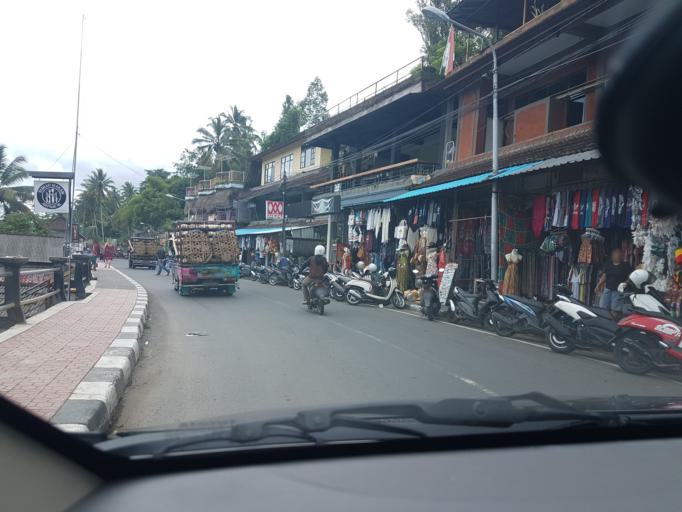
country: ID
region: Bali
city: Tegalalang
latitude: -8.4324
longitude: 115.2785
